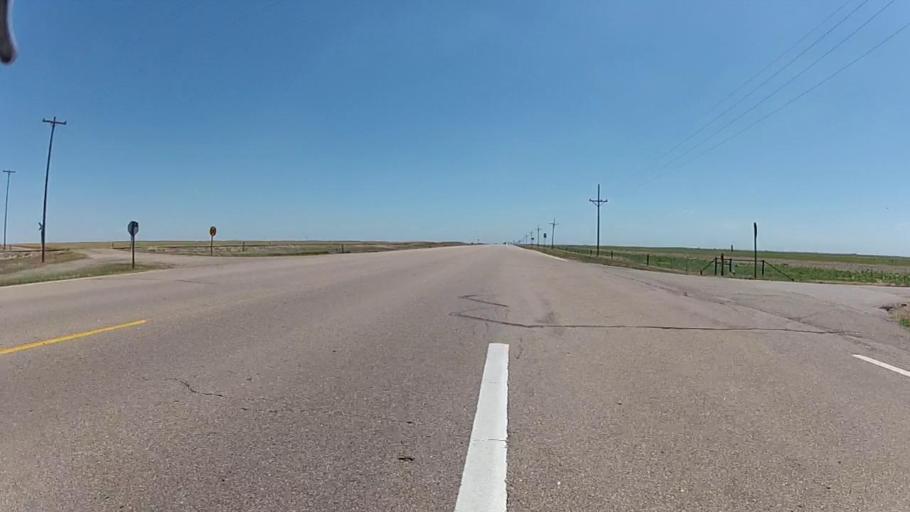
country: US
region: Kansas
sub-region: Ford County
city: Dodge City
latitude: 37.7132
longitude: -100.1064
